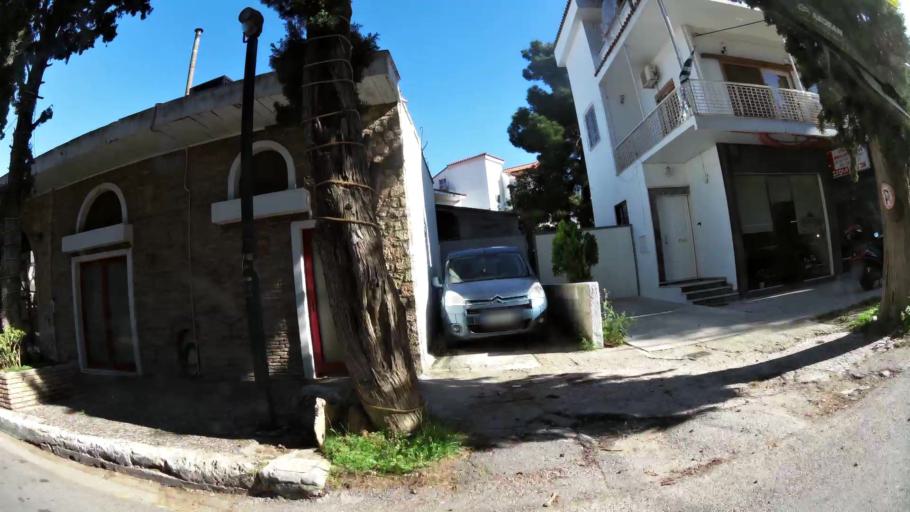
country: GR
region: Attica
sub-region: Nomarchia Anatolikis Attikis
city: Anoixi
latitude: 38.1315
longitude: 23.8616
